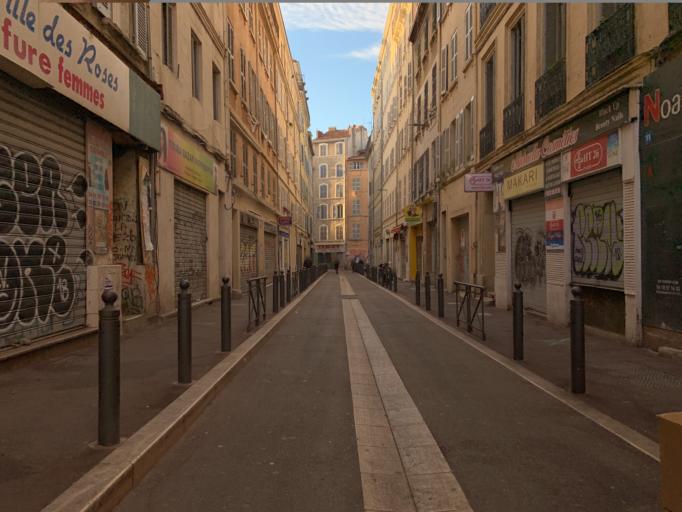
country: FR
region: Provence-Alpes-Cote d'Azur
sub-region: Departement des Bouches-du-Rhone
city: Marseille
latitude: 43.2960
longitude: 5.3801
